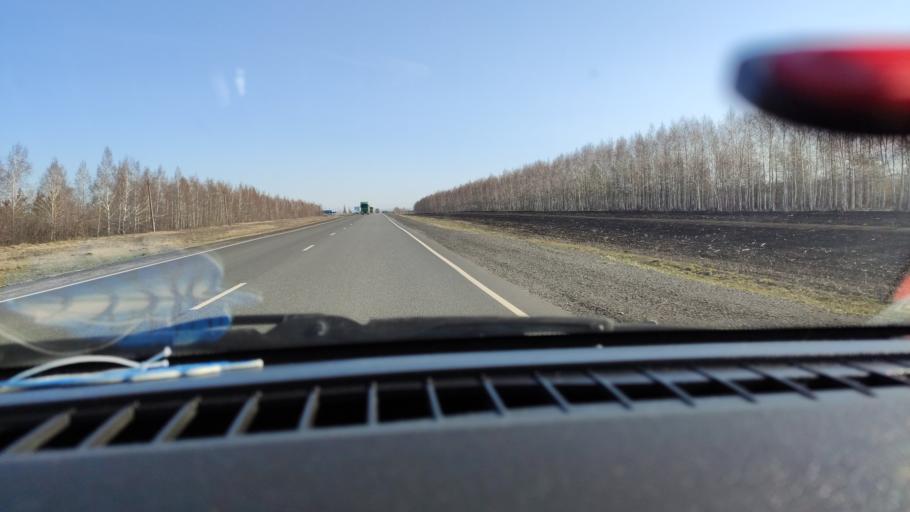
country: RU
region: Samara
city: Syzran'
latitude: 52.9908
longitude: 48.3215
